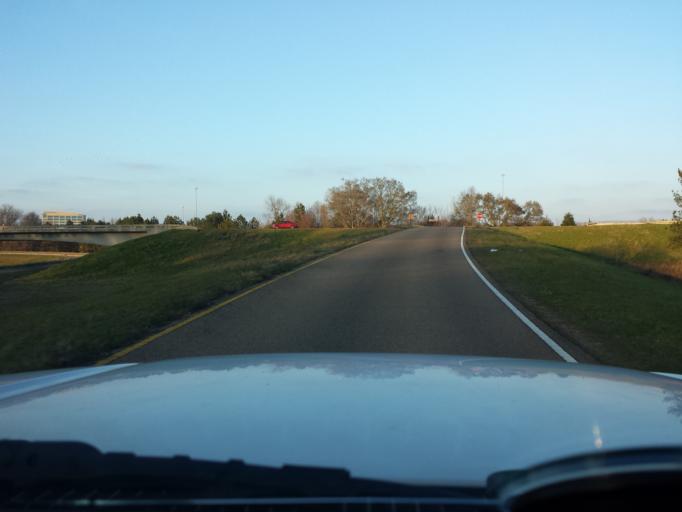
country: US
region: Mississippi
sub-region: Madison County
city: Ridgeland
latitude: 32.4276
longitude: -90.1458
